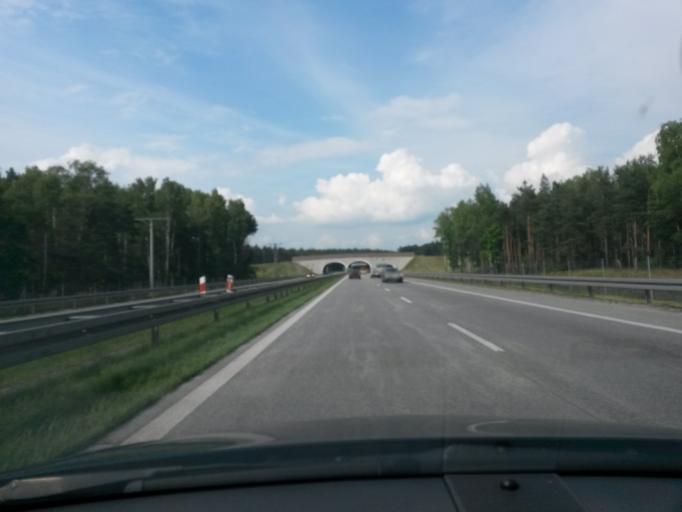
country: PL
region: Lodz Voivodeship
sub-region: Powiat tomaszowski
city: Lubochnia
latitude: 51.5757
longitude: 20.0281
